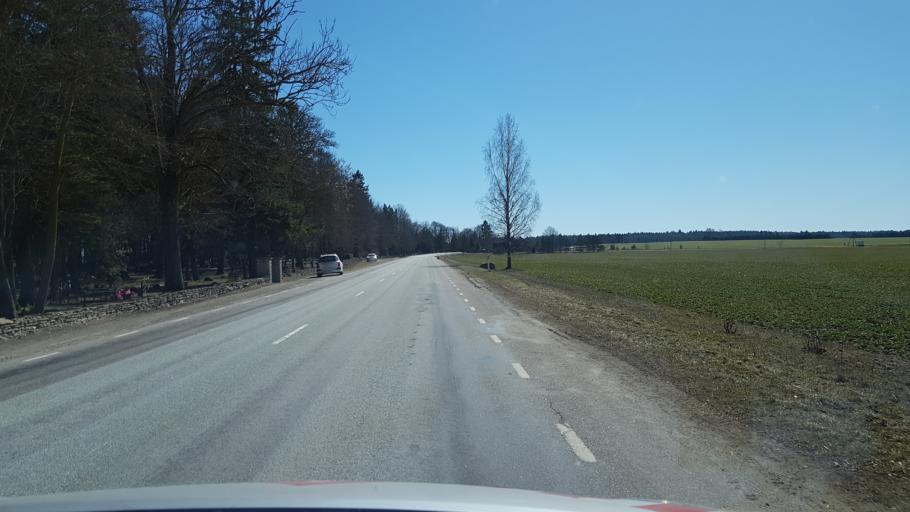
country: EE
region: Laeaene-Virumaa
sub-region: Viru-Nigula vald
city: Kunda
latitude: 59.4394
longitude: 26.6972
